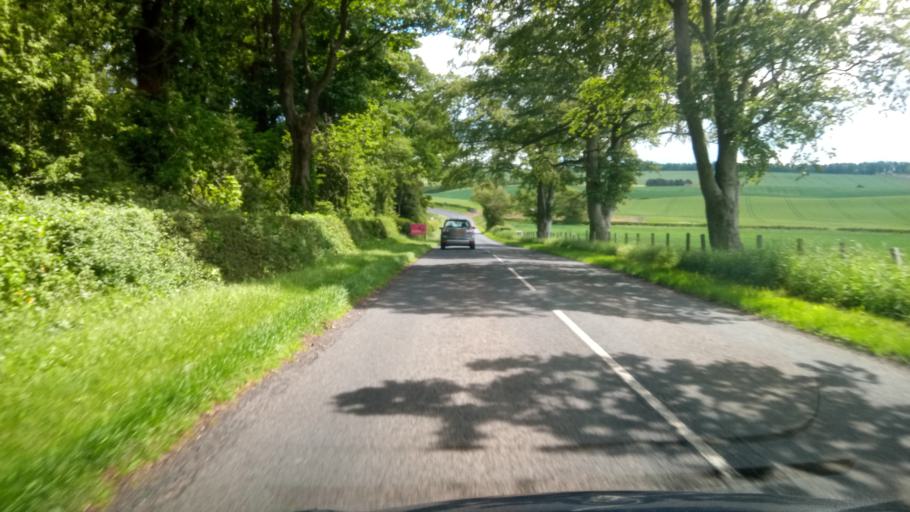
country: GB
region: Scotland
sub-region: The Scottish Borders
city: Coldstream
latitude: 55.6042
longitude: -2.3073
